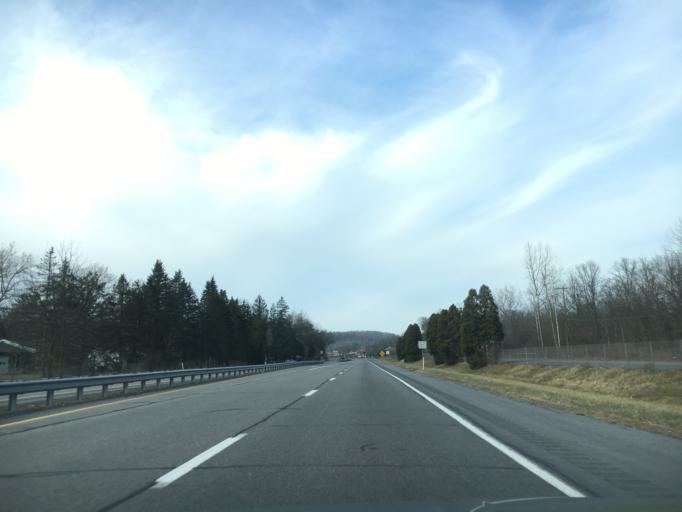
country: US
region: Pennsylvania
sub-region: Montour County
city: Danville
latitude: 40.9894
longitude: -76.6344
